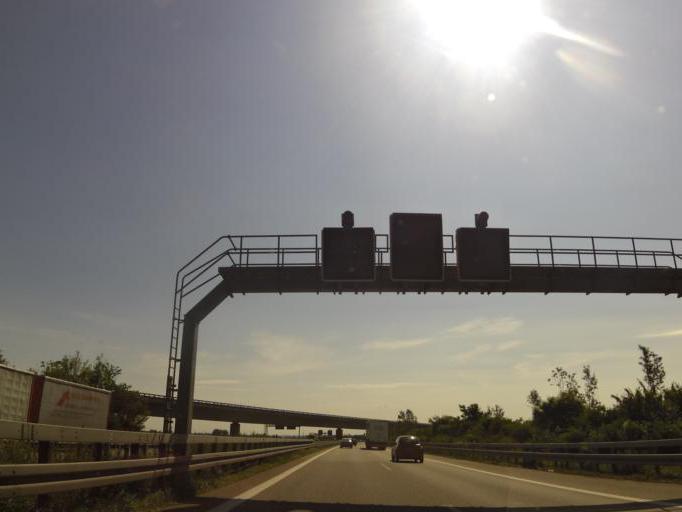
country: DE
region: Baden-Wuerttemberg
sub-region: Tuebingen Region
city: Langenau
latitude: 48.4652
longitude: 10.1115
